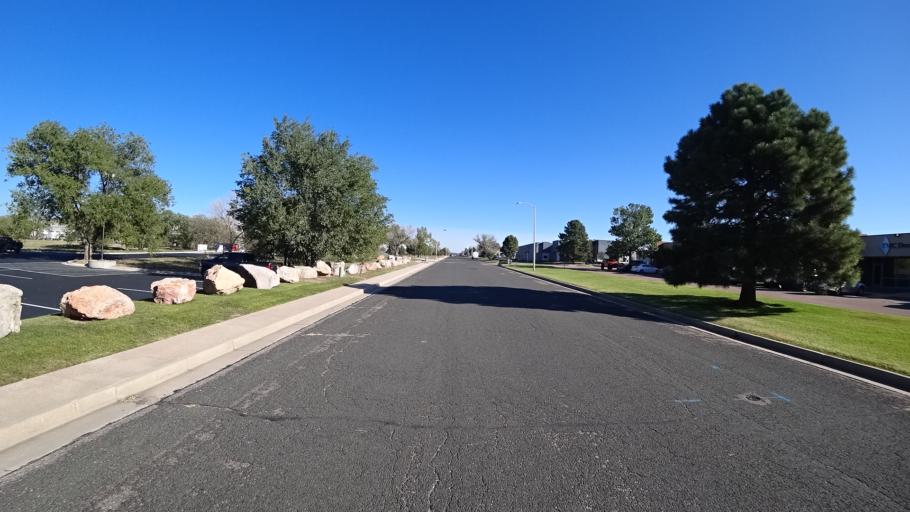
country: US
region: Colorado
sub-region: El Paso County
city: Cimarron Hills
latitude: 38.8092
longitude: -104.7253
